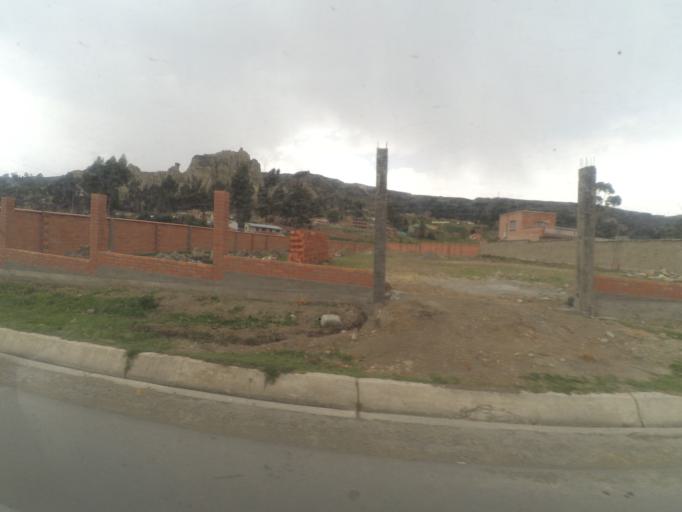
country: BO
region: La Paz
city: La Paz
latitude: -16.5744
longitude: -68.1704
